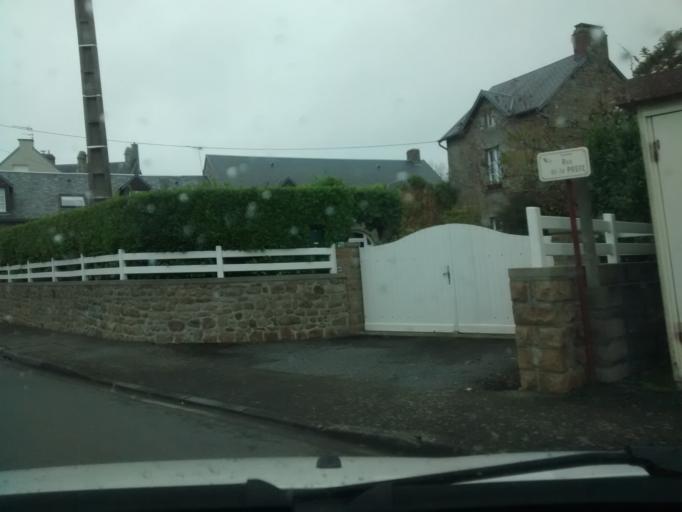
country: FR
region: Lower Normandy
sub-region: Departement de la Manche
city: Jullouville
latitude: 48.7482
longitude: -1.5583
